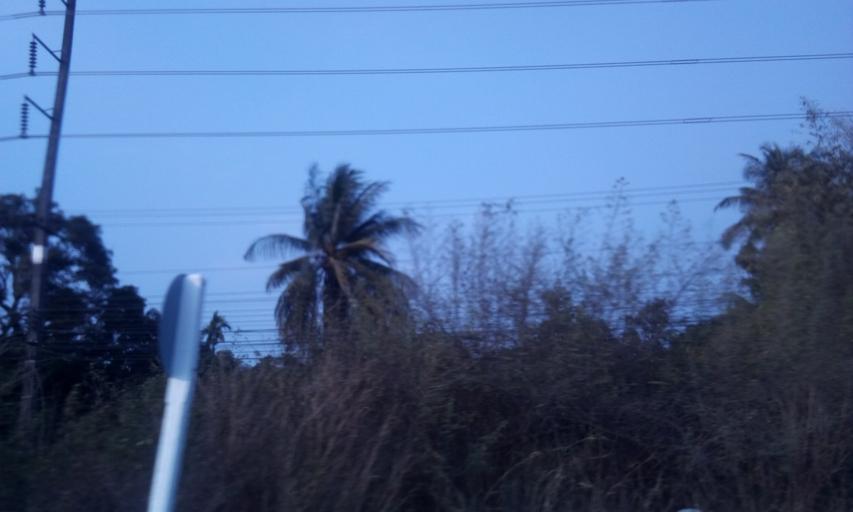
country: TH
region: Chanthaburi
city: Khlung
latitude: 12.4561
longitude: 102.2369
